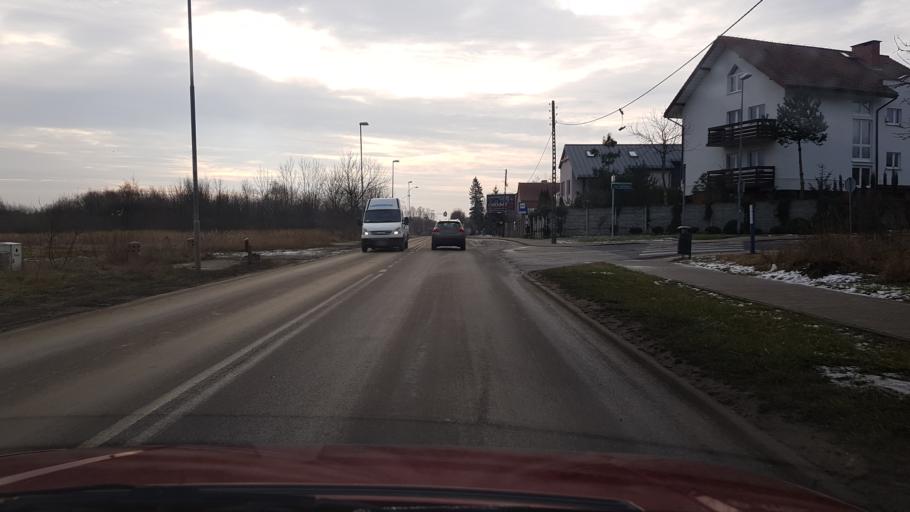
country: PL
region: West Pomeranian Voivodeship
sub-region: Powiat policki
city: Police
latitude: 53.4951
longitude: 14.5834
